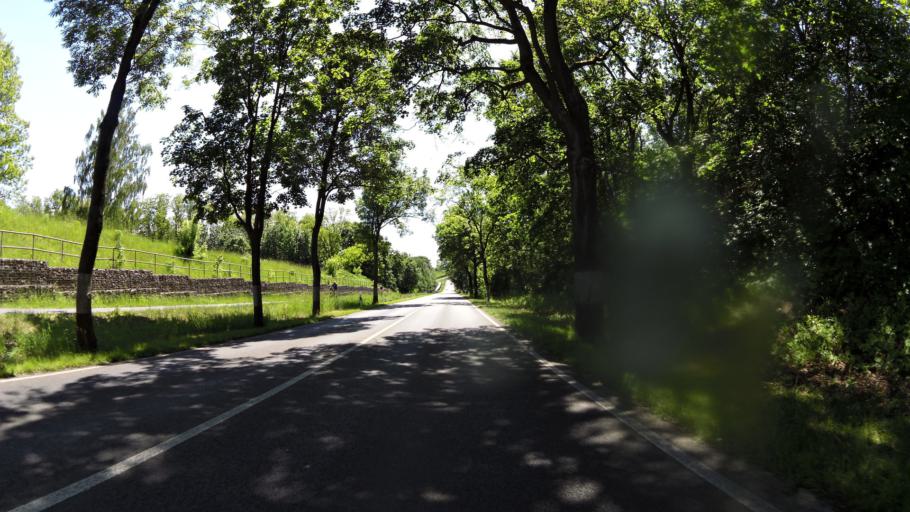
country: DE
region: Brandenburg
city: Lebus
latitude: 52.4106
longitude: 14.5256
